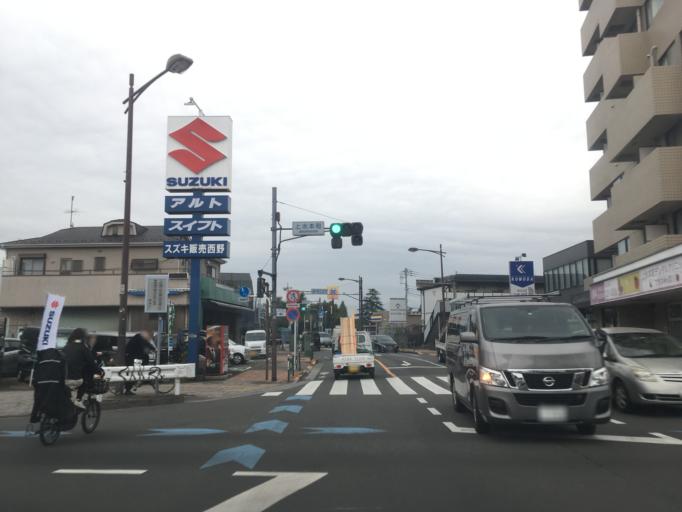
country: JP
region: Tokyo
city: Kokubunji
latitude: 35.7174
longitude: 139.4652
